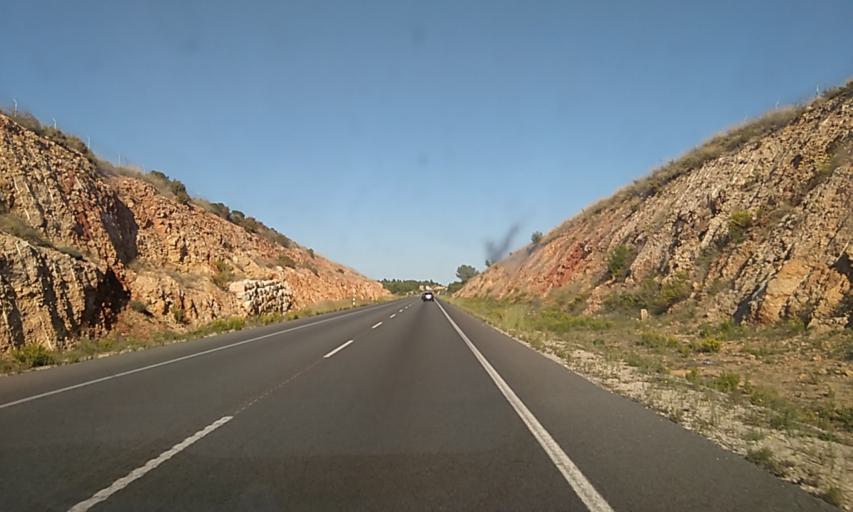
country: ES
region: Valencia
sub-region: Provincia de Castello
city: Torreblanca
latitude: 40.2152
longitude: 0.1524
